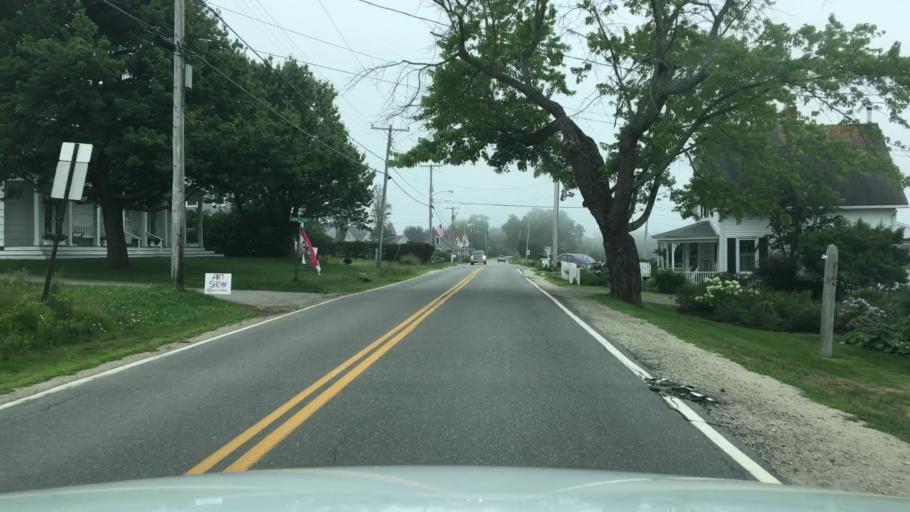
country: US
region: Maine
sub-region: Cumberland County
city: Harpswell Center
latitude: 43.7328
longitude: -69.9955
